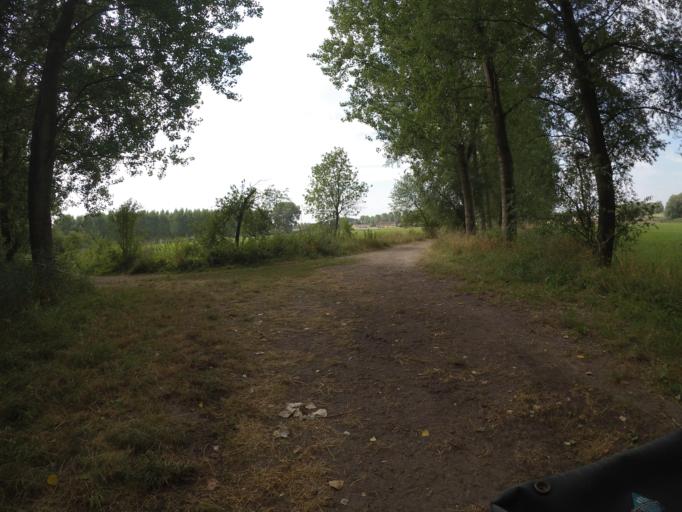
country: NL
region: North Brabant
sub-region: Gemeente Schijndel
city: Schijndel
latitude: 51.6438
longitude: 5.4460
